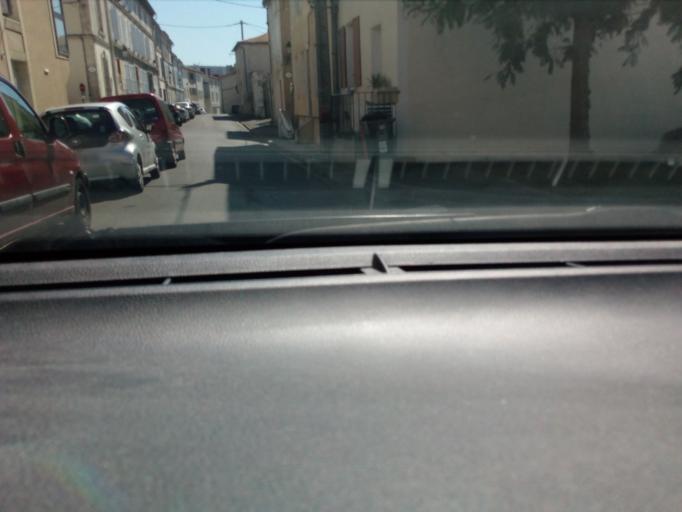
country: FR
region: Poitou-Charentes
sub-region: Departement de la Charente
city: Angouleme
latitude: 45.6580
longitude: 0.1614
